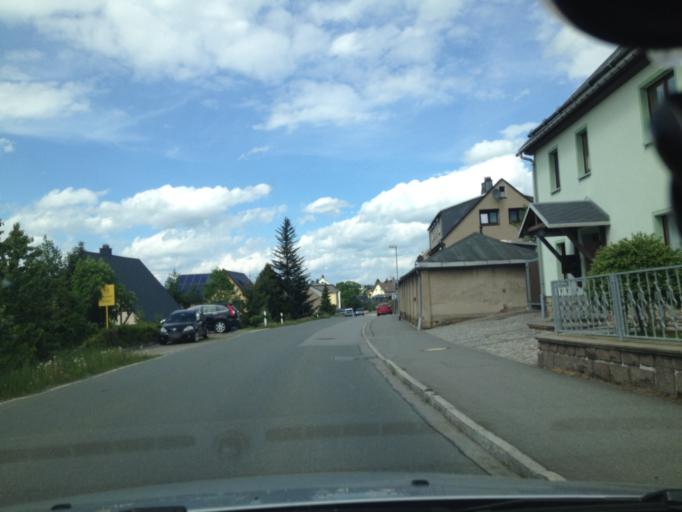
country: DE
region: Saxony
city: Barenstein
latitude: 50.5246
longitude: 12.9958
